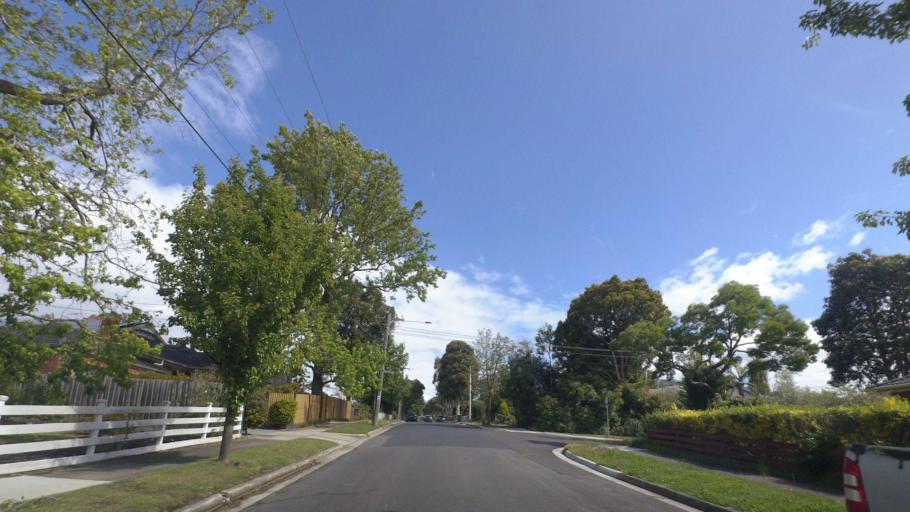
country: AU
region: Victoria
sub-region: Whitehorse
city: Vermont
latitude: -37.8294
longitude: 145.1989
